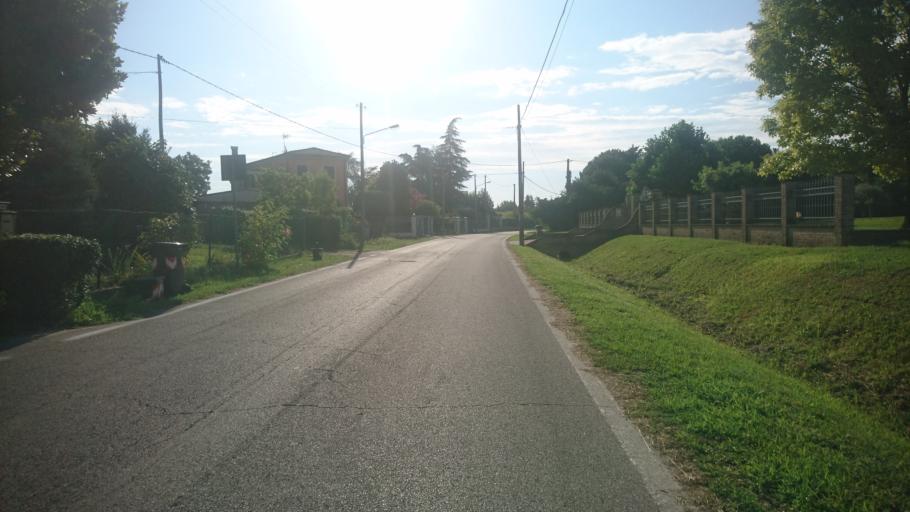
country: IT
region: Veneto
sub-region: Provincia di Padova
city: Villaguattera
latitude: 45.4347
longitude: 11.8318
